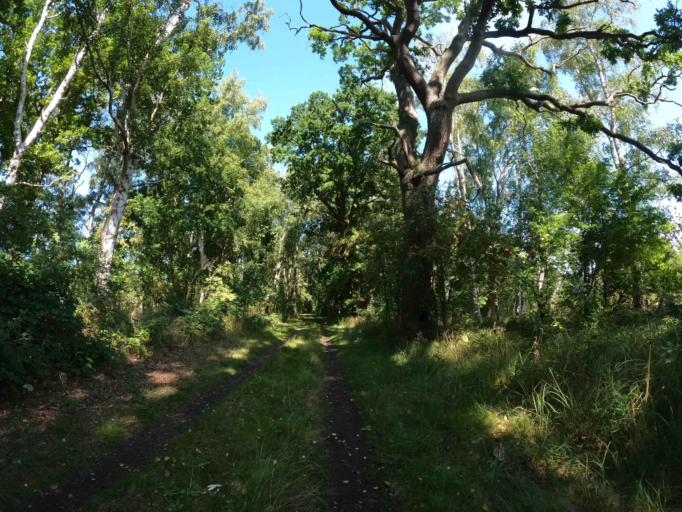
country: DE
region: Mecklenburg-Vorpommern
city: Prohn
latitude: 54.4291
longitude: 13.0308
